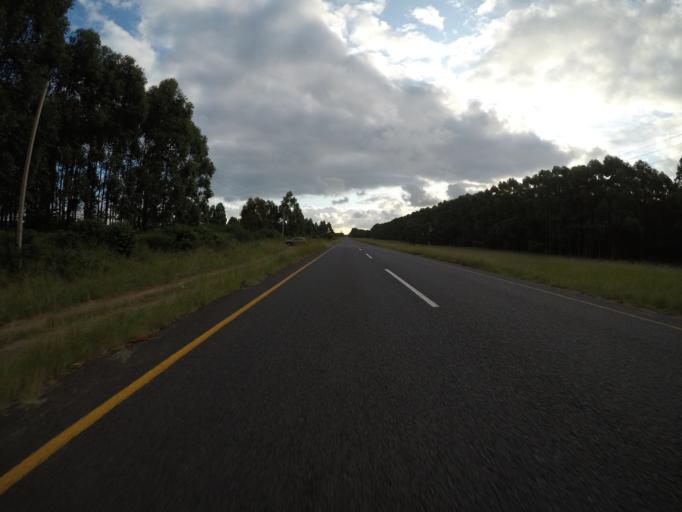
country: ZA
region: KwaZulu-Natal
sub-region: uMkhanyakude District Municipality
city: Mtubatuba
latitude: -28.3933
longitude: 32.2227
